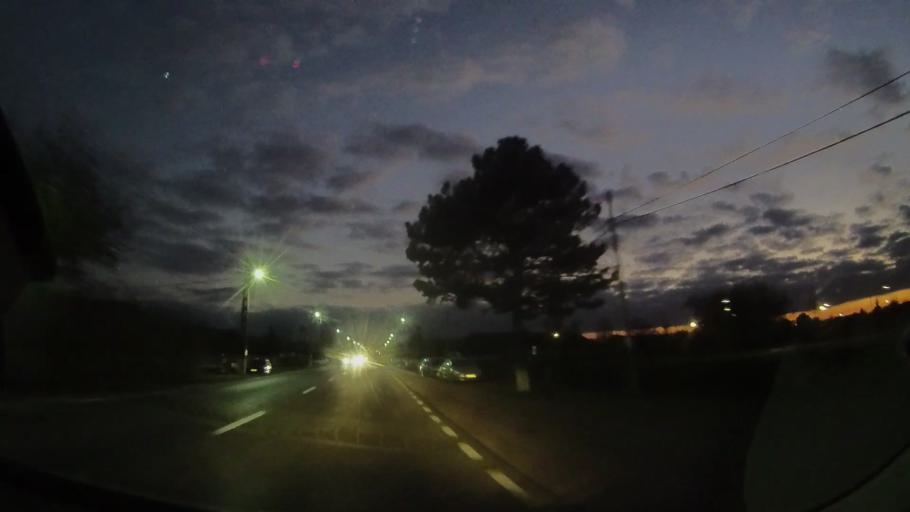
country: RO
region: Tulcea
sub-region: Comuna Mihail Kogalniceanu
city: Mihail Kogalniceanu
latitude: 45.0428
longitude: 28.7353
